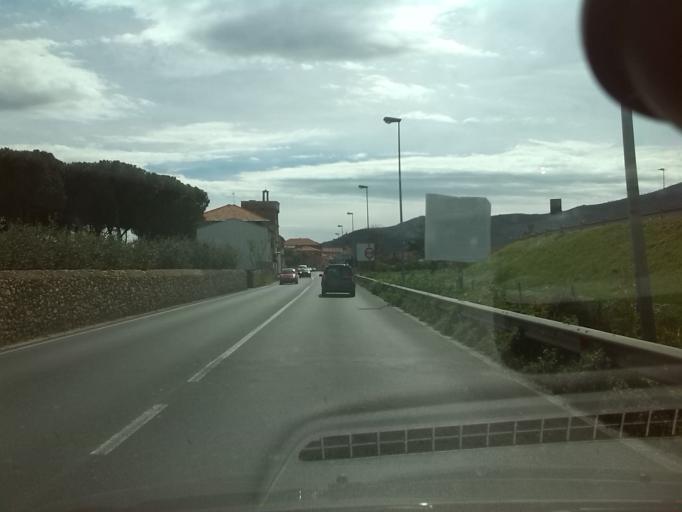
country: IT
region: Liguria
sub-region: Provincia di Savona
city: San Fedele-Lusignano
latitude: 44.0650
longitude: 8.1770
